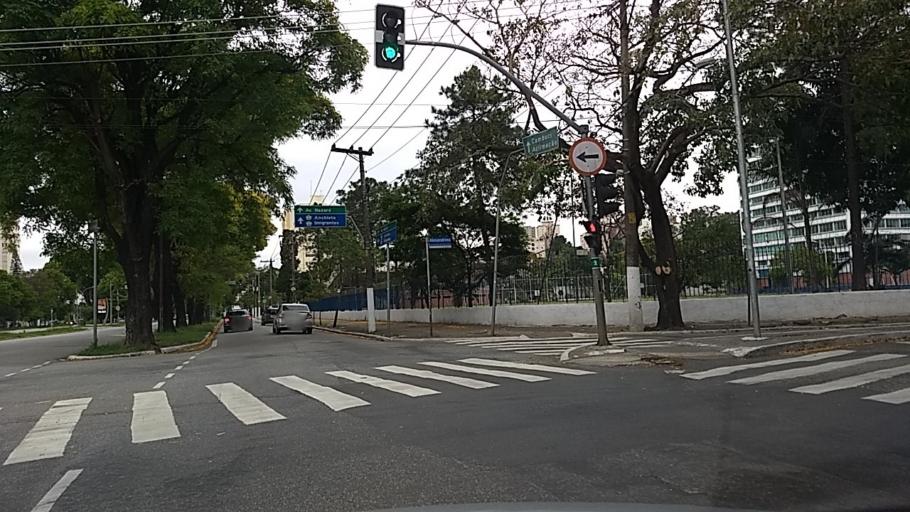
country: BR
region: Sao Paulo
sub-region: Sao Paulo
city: Sao Paulo
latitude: -23.5646
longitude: -46.6118
